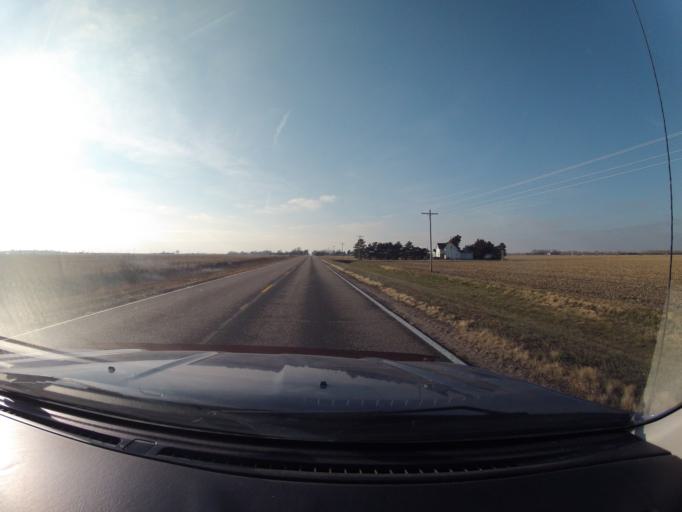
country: US
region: Nebraska
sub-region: Buffalo County
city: Kearney
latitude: 40.6410
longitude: -99.0728
